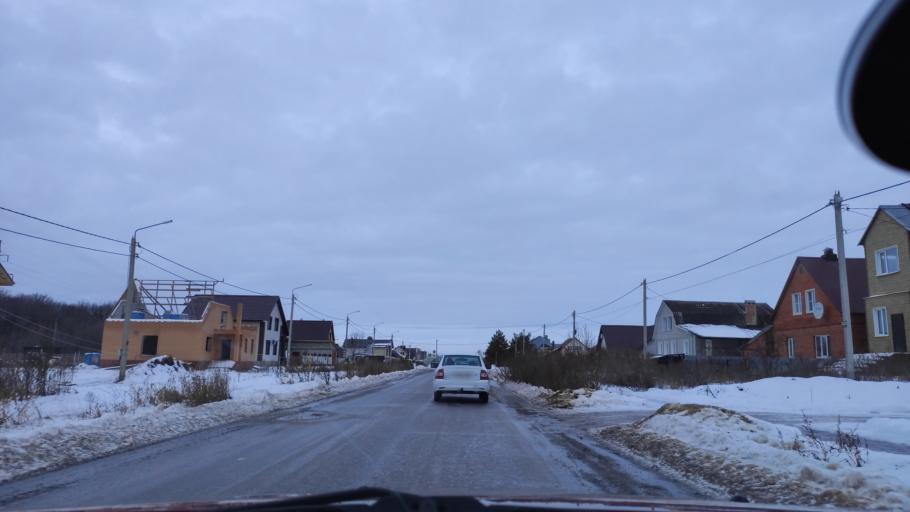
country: RU
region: Tambov
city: Tambov
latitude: 52.7592
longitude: 41.3692
